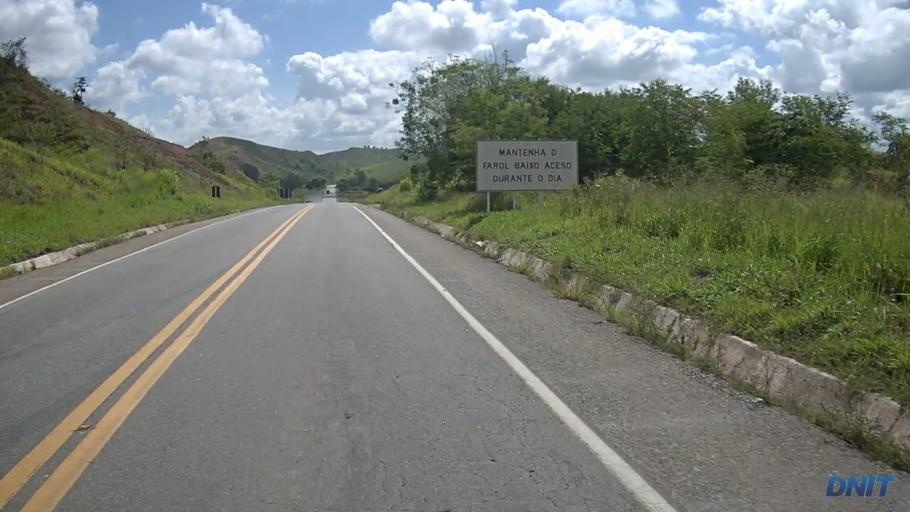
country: BR
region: Minas Gerais
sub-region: Belo Oriente
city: Belo Oriente
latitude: -19.1447
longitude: -42.2286
